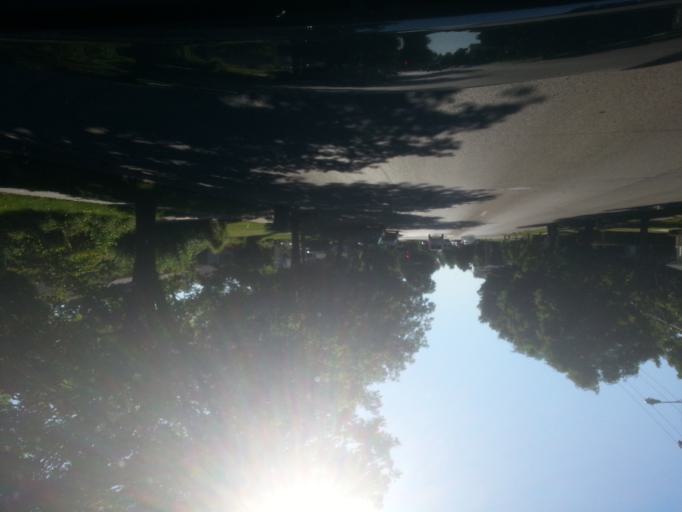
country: US
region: Wisconsin
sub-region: Dane County
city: Shorewood Hills
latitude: 43.0499
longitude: -89.4527
